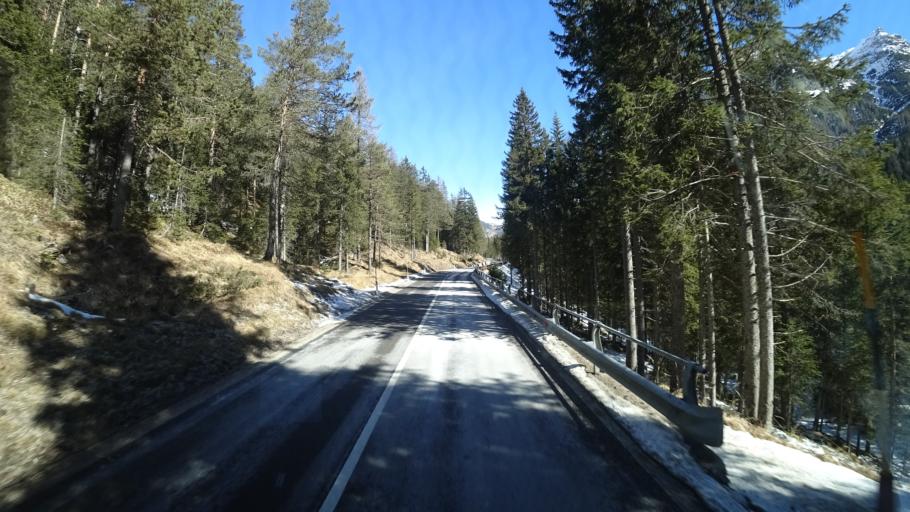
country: IT
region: Veneto
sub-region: Provincia di Belluno
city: Cortina d'Ampezzo
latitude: 46.6063
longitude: 12.1492
